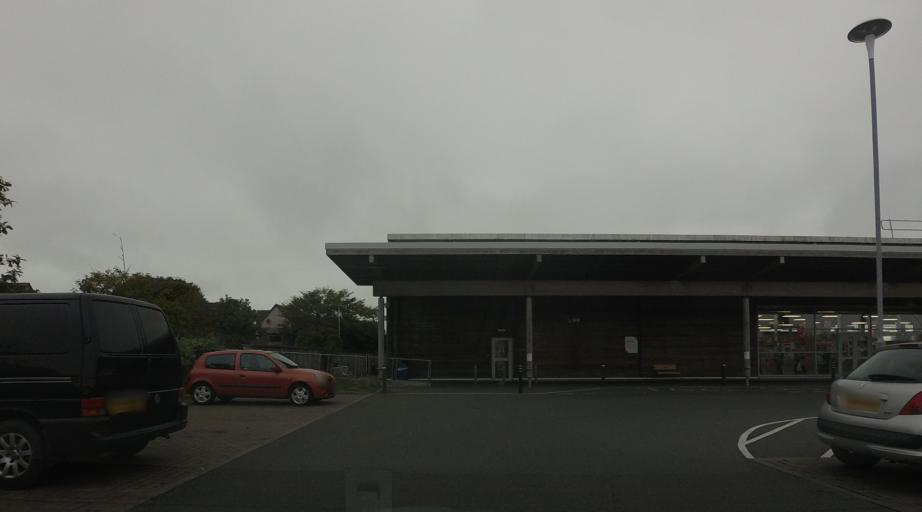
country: GB
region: Scotland
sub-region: Orkney Islands
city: Orkney
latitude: 58.9803
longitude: -2.9671
